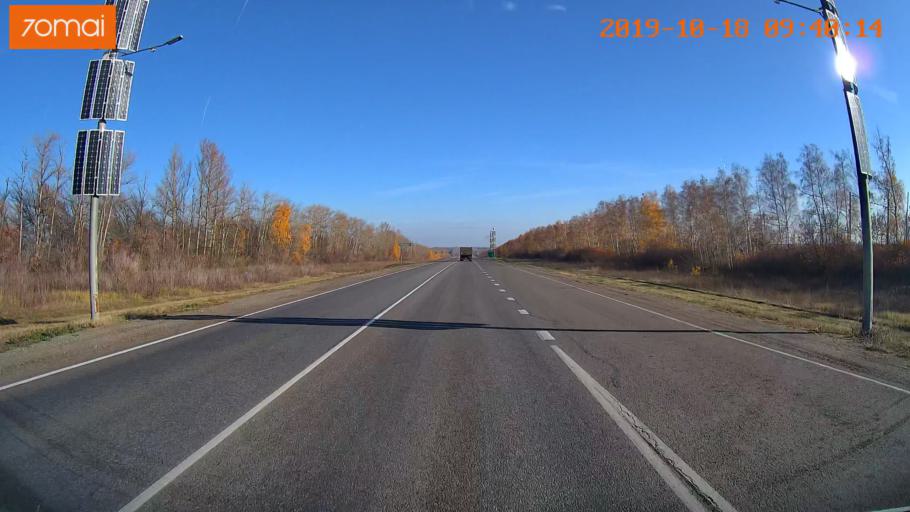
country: RU
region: Tula
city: Yefremov
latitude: 53.2618
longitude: 38.1454
